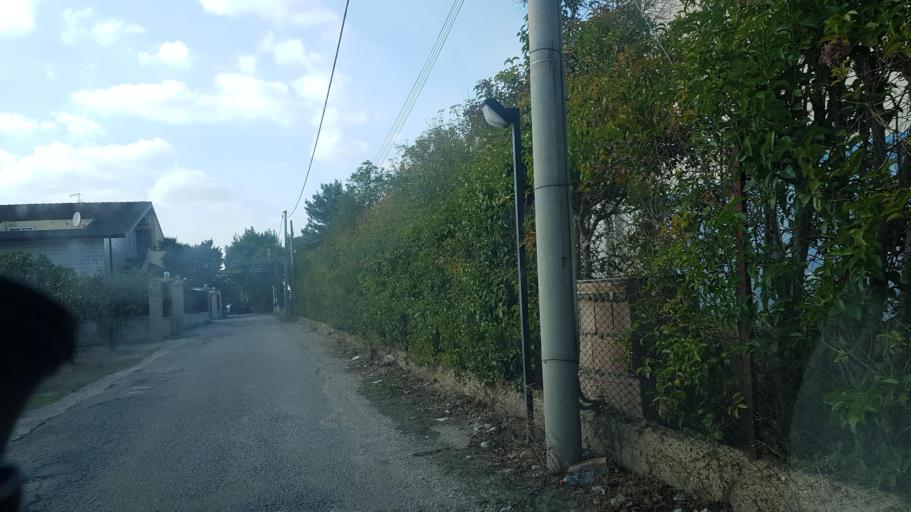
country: IT
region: Apulia
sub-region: Provincia di Foggia
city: Foggia
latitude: 41.4414
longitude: 15.5226
